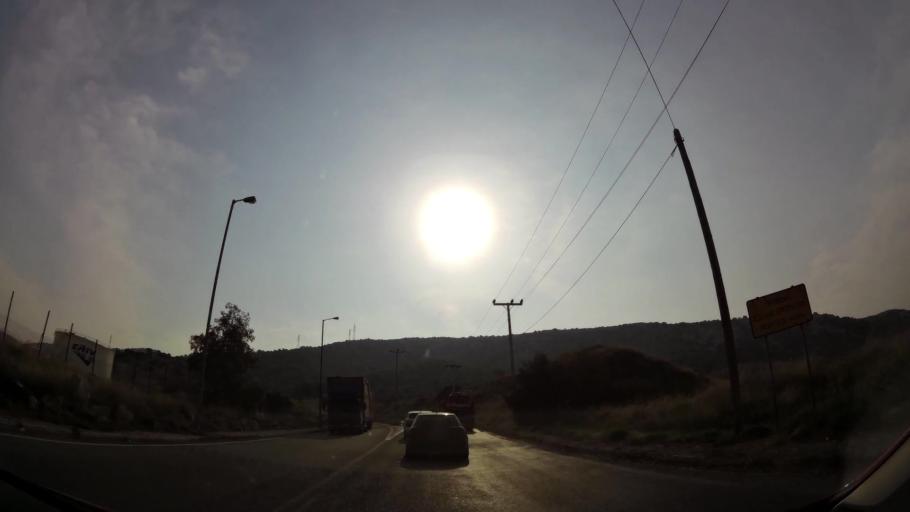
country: GR
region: Attica
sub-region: Nomarchia Athinas
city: Skaramangas
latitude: 38.0261
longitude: 23.6119
